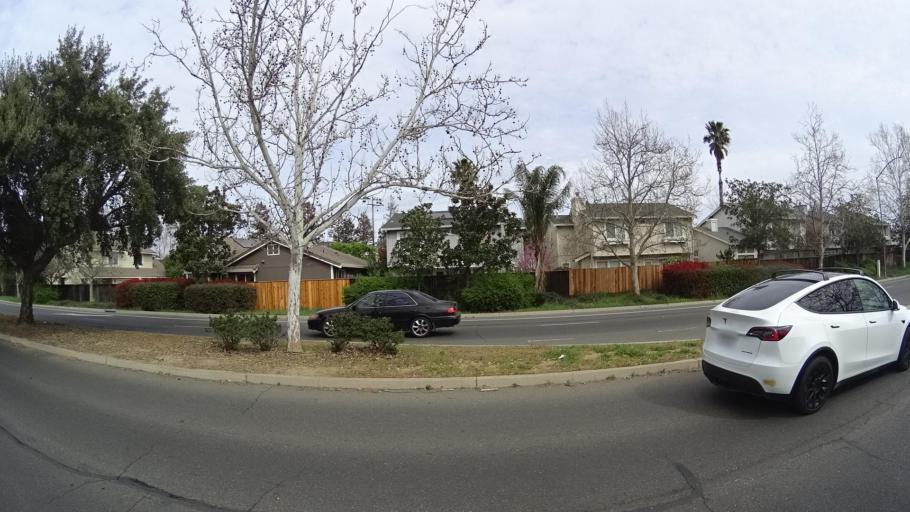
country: US
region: California
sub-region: Yolo County
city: Davis
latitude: 38.5425
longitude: -121.7251
